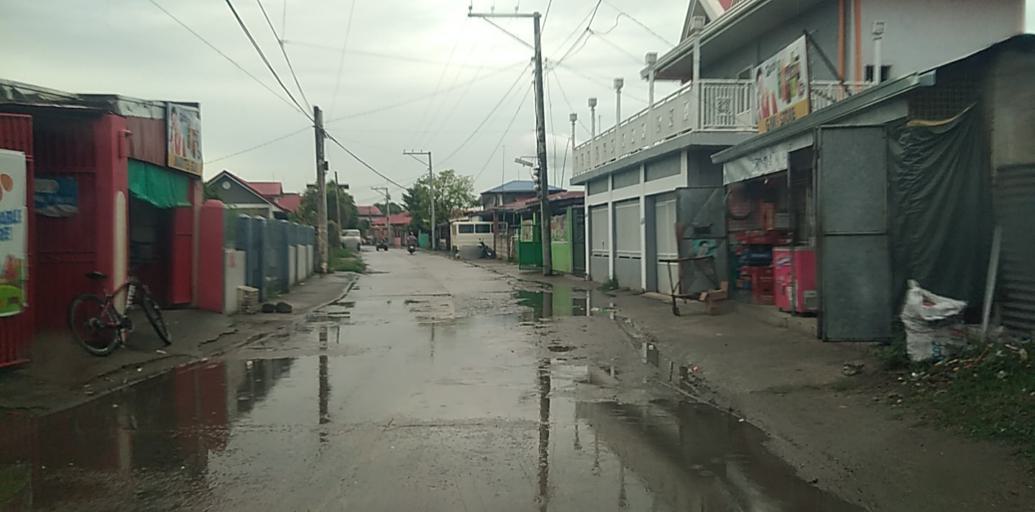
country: PH
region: Central Luzon
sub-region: Province of Pampanga
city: Arayat
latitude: 15.1379
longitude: 120.7391
